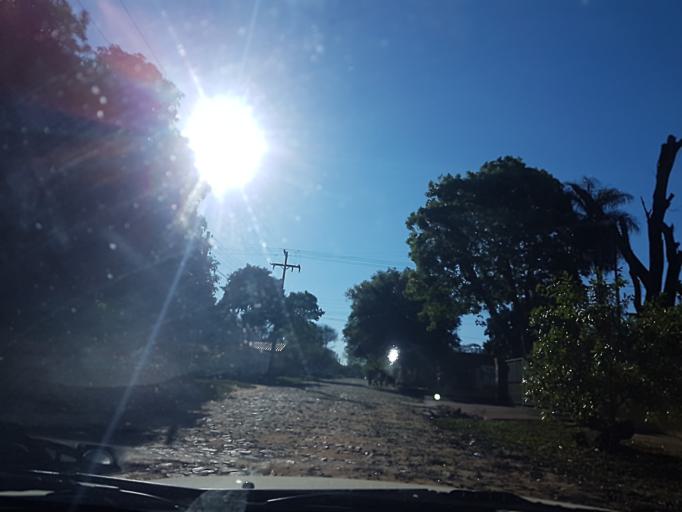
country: PY
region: Central
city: San Lorenzo
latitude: -25.2767
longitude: -57.4640
